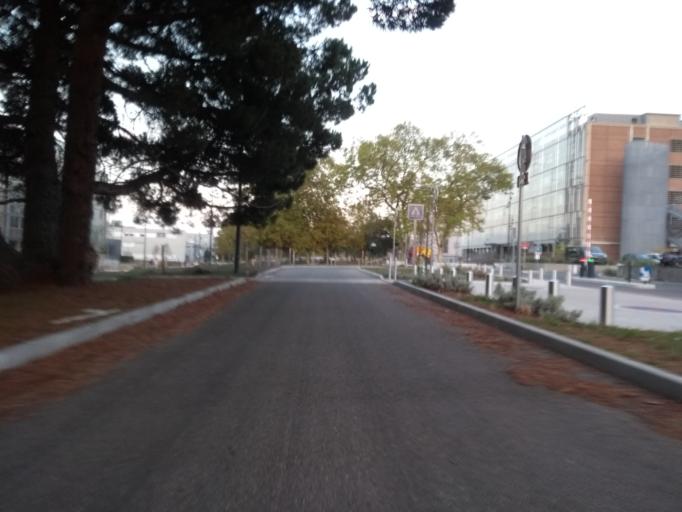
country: FR
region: Aquitaine
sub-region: Departement de la Gironde
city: Talence
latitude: 44.8066
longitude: -0.5994
